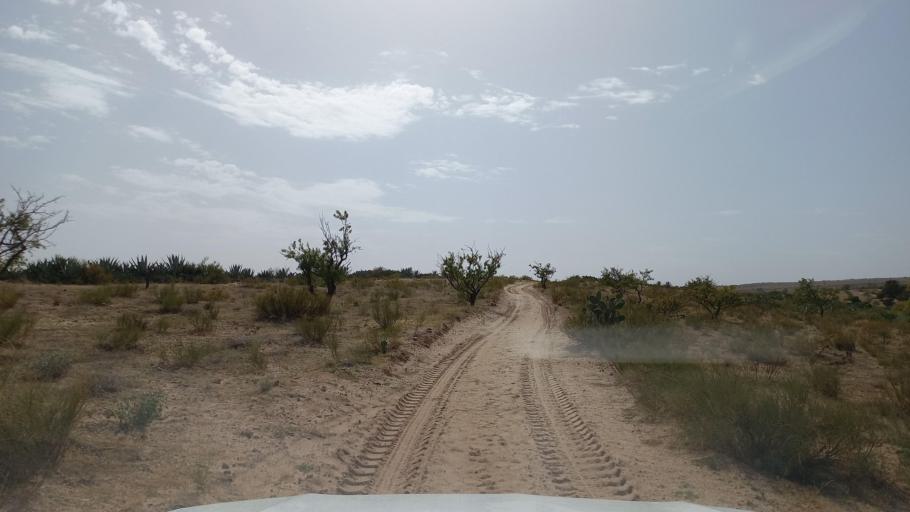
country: TN
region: Al Qasrayn
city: Kasserine
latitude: 35.2997
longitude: 8.9455
